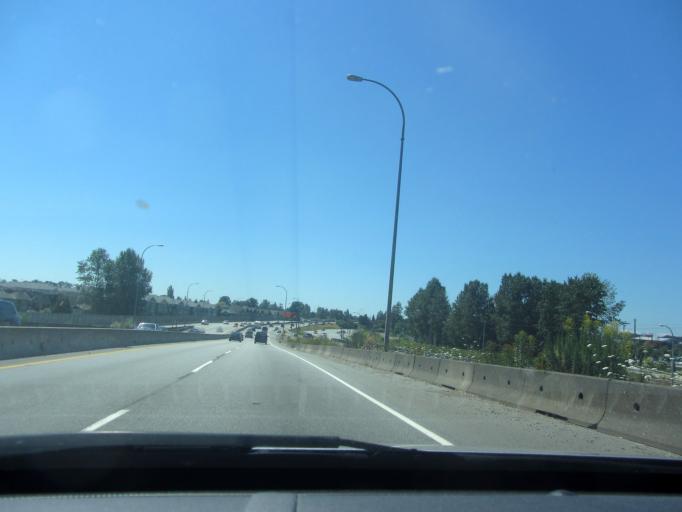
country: CA
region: British Columbia
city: New Westminster
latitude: 49.1875
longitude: -122.9492
